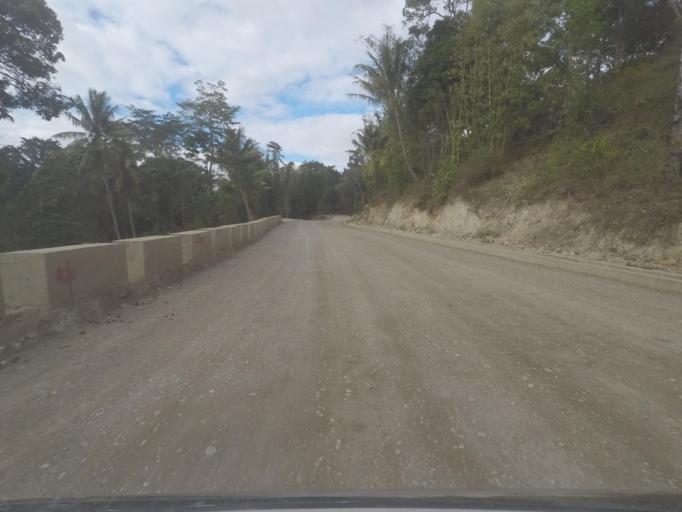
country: TL
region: Baucau
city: Venilale
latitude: -8.6239
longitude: 126.3828
